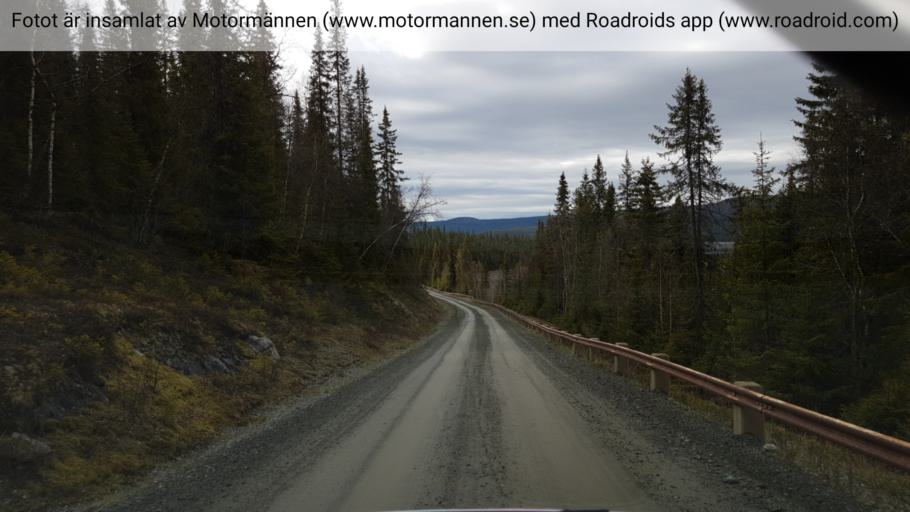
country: SE
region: Vaesterbotten
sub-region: Vilhelmina Kommun
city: Sjoberg
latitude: 65.5348
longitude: 15.4338
